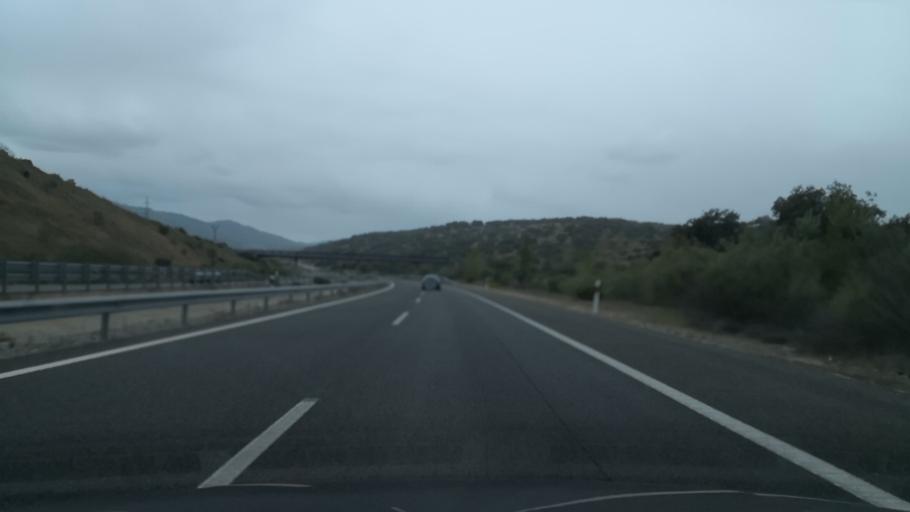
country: ES
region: Extremadura
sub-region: Provincia de Caceres
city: Villar de Plasencia
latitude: 40.1355
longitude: -6.0456
